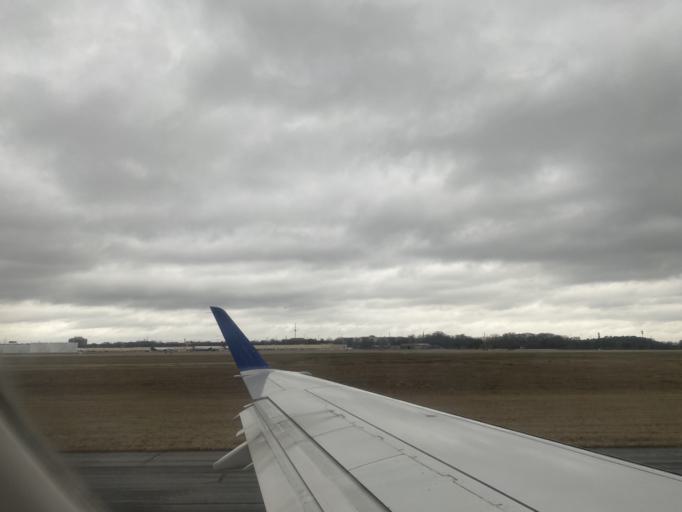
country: US
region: Georgia
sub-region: Fulton County
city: Hapeville
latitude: 33.6453
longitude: -84.4113
